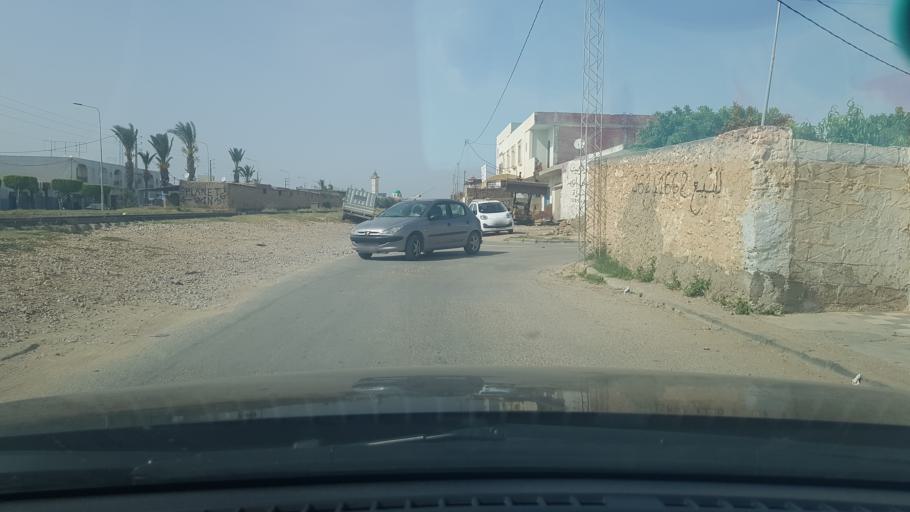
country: TN
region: Safaqis
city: Al Qarmadah
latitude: 34.8184
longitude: 10.7626
